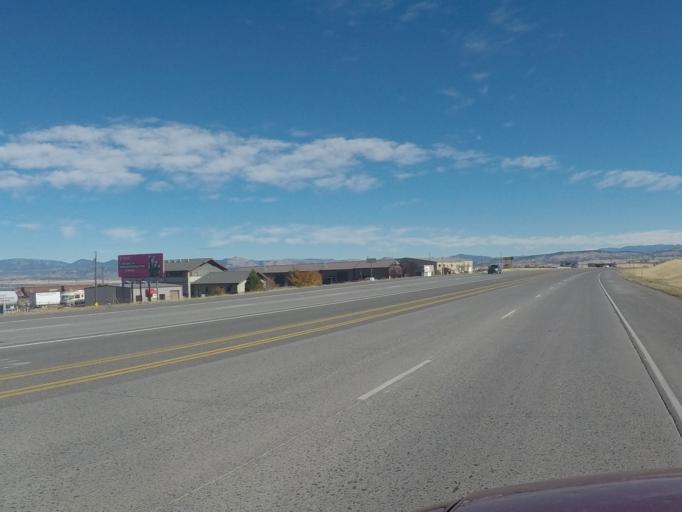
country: US
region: Montana
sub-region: Lewis and Clark County
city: East Helena
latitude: 46.5908
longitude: -111.9634
